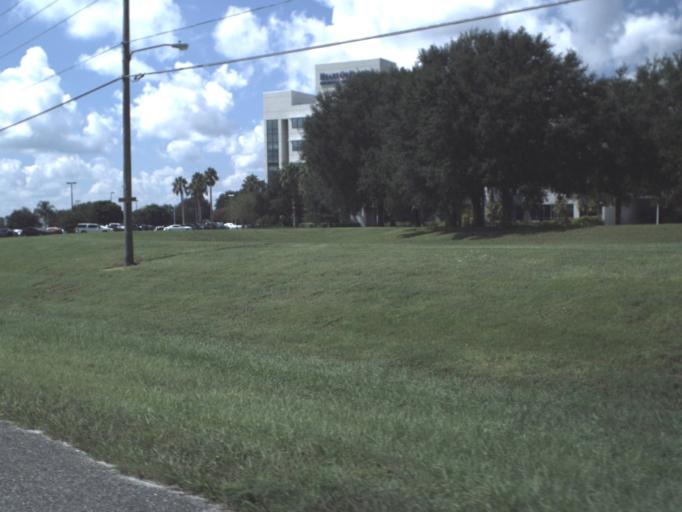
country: US
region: Florida
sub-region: Polk County
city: Davenport
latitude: 28.1827
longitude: -81.6400
